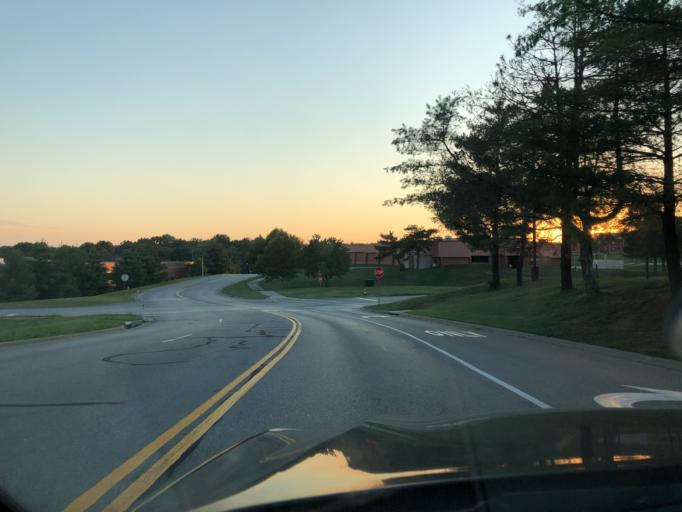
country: US
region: Kansas
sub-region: Leavenworth County
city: Leavenworth
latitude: 39.3411
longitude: -94.9230
